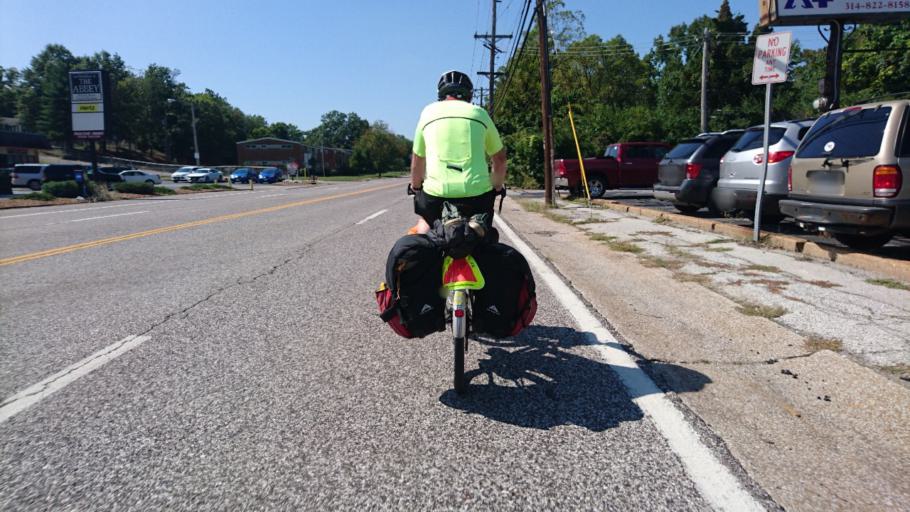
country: US
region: Missouri
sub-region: Saint Louis County
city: Warson Woods
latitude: 38.6021
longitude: -90.3903
